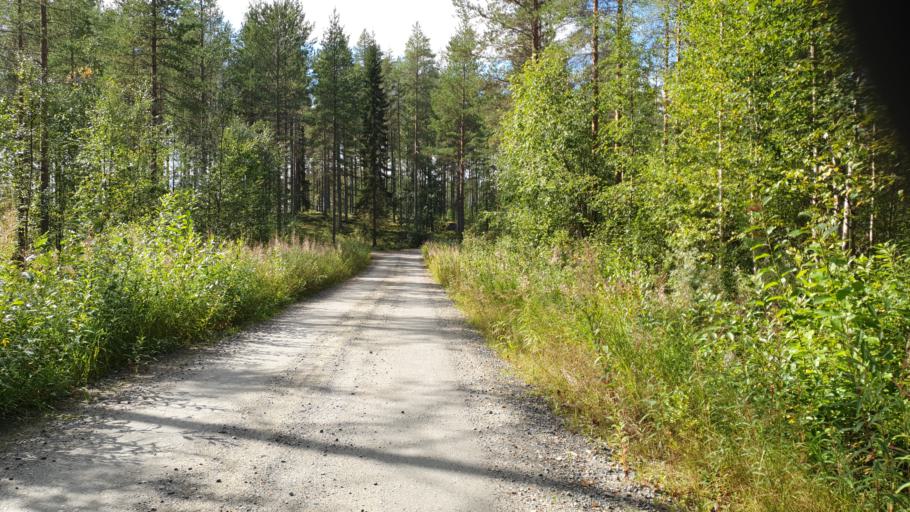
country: FI
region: Kainuu
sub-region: Kehys-Kainuu
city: Kuhmo
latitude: 64.1306
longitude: 29.3498
